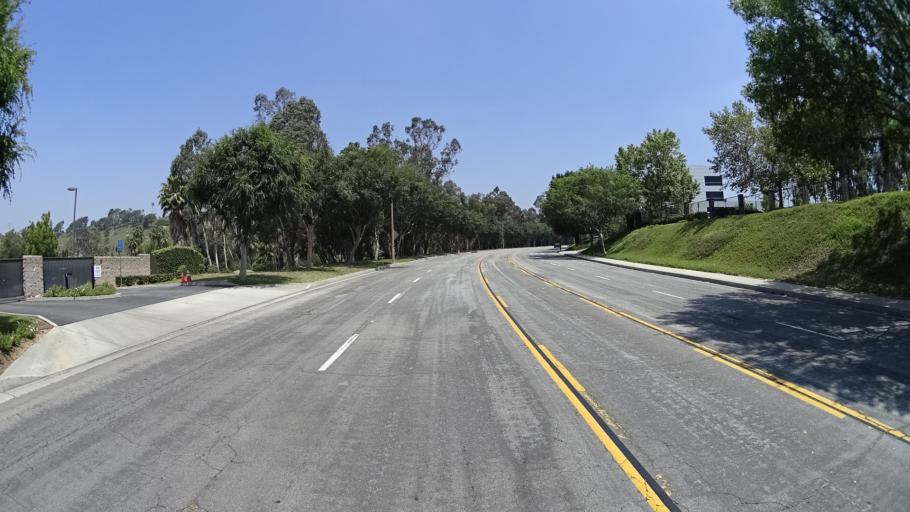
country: US
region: California
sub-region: Los Angeles County
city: Belvedere
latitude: 34.0450
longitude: -118.1671
